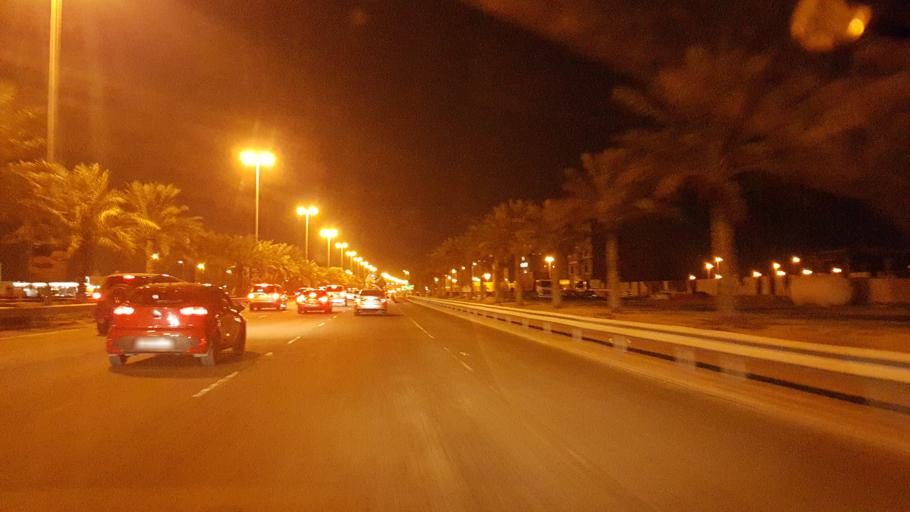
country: BH
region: Muharraq
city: Al Hadd
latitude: 26.2396
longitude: 50.6580
